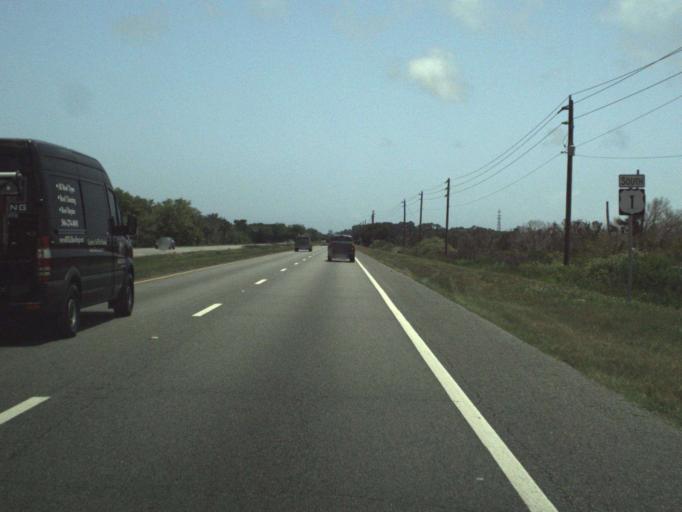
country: US
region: Florida
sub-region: Volusia County
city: Ormond Beach
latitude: 29.2986
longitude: -81.0845
